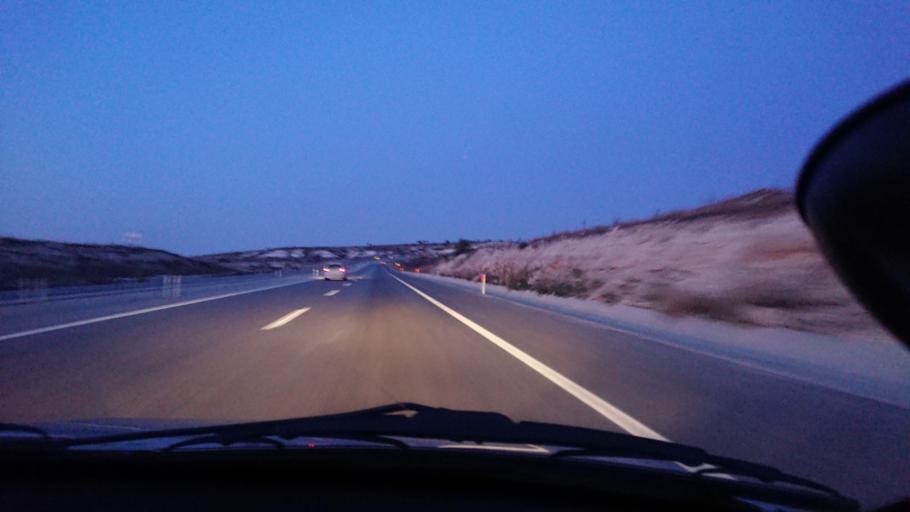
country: TR
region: Kuetahya
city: Cavdarhisar
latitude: 39.1369
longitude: 29.5585
